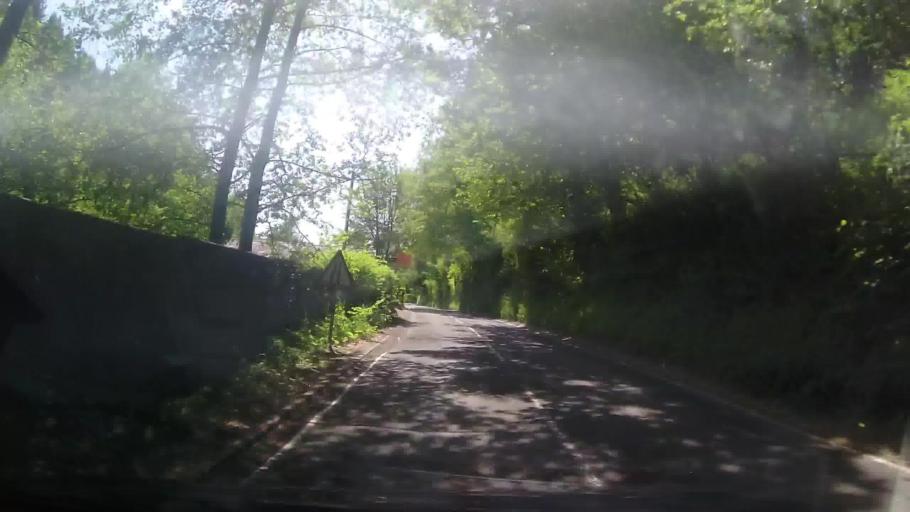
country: GB
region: Wales
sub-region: Monmouthshire
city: Monmouth
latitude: 51.8448
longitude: -2.7184
